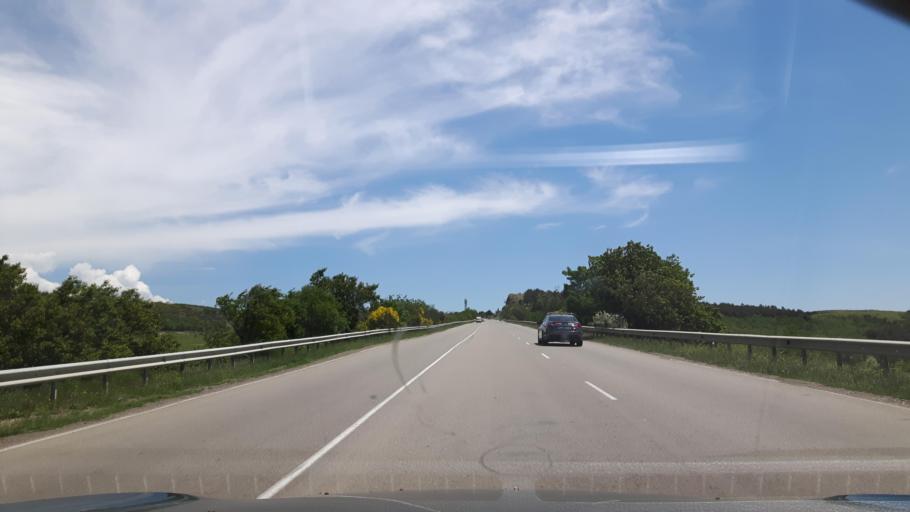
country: GE
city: Didi Lilo
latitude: 41.6924
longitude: 45.0693
